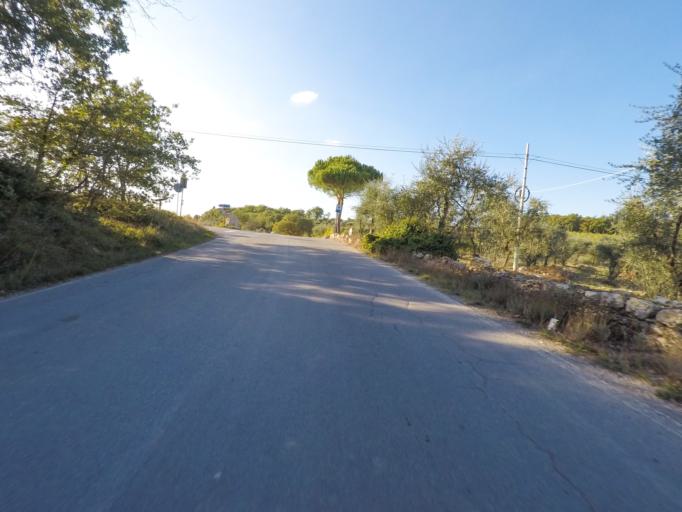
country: IT
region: Tuscany
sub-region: Provincia di Siena
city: Radda in Chianti
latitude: 43.4513
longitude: 11.3910
